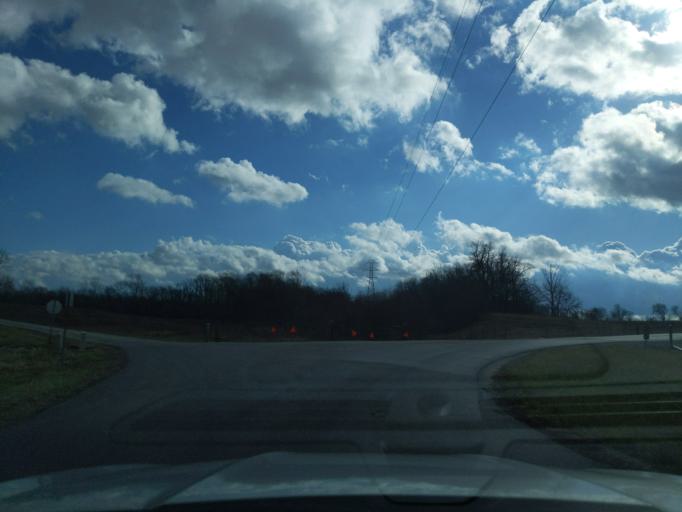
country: US
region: Indiana
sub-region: Decatur County
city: Greensburg
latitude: 39.3951
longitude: -85.5082
